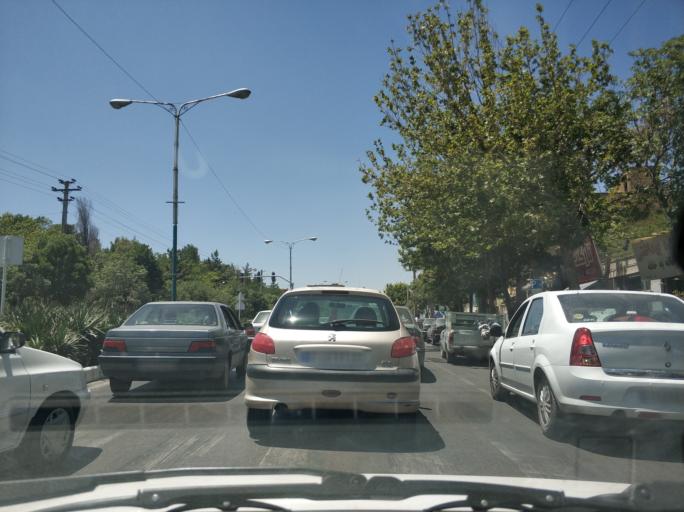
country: IR
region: Razavi Khorasan
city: Mashhad
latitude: 36.3105
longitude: 59.4979
